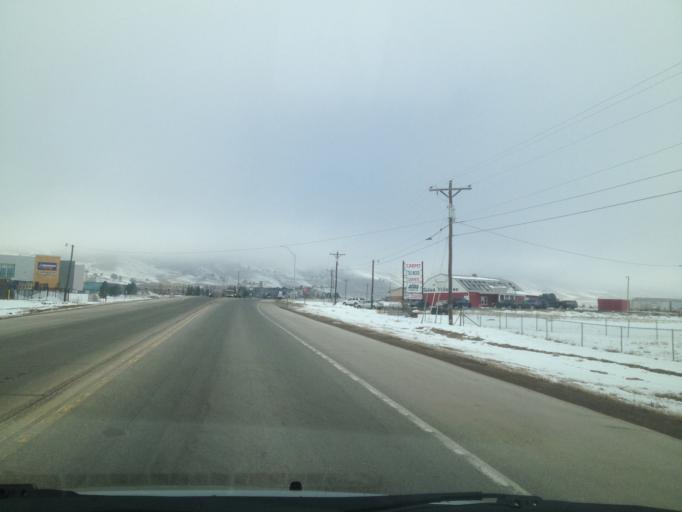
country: US
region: Colorado
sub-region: Boulder County
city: Boulder
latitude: 40.0634
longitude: -105.2789
